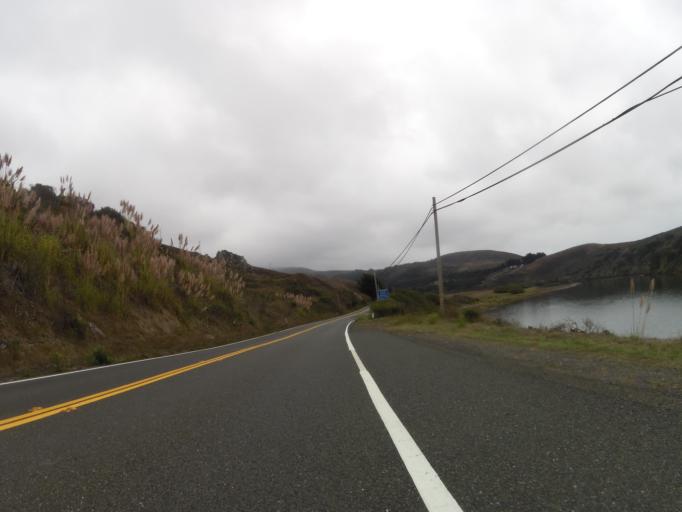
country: US
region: California
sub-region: Sonoma County
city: Monte Rio
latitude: 38.4453
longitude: -123.1116
